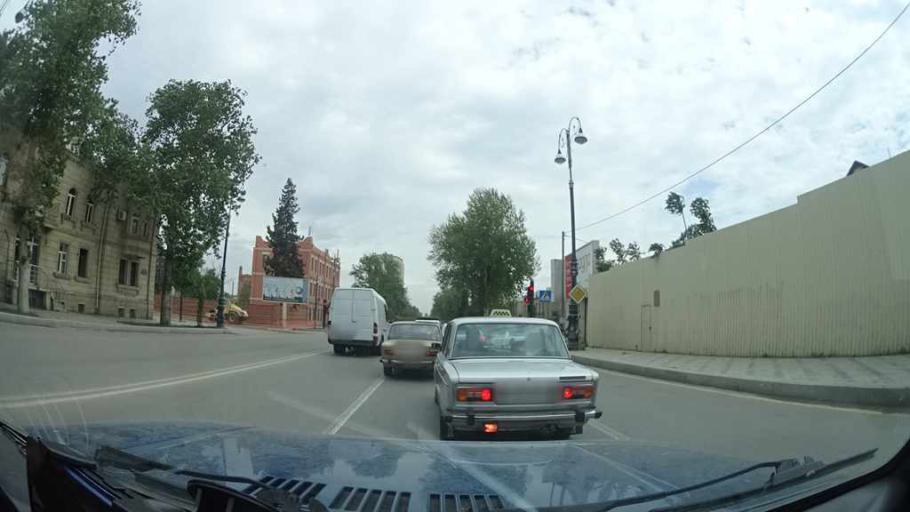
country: AZ
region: Ganja City
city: Ganja
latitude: 40.6855
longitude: 46.3631
